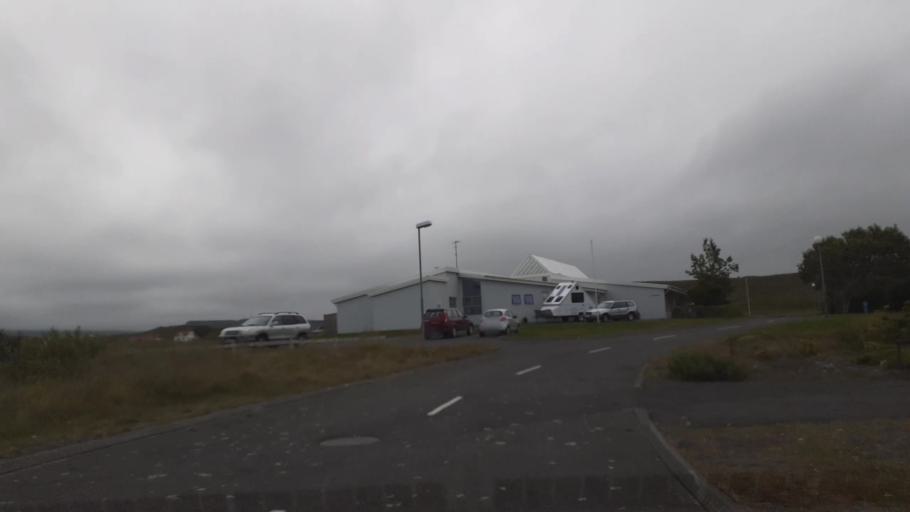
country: IS
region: Northwest
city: Saudarkrokur
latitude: 65.6568
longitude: -20.2787
